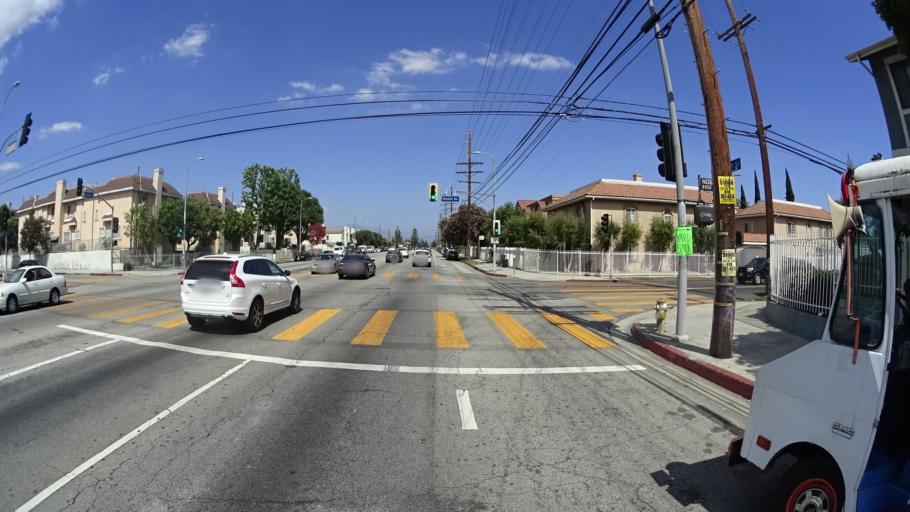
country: US
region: California
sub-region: Los Angeles County
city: Van Nuys
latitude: 34.2354
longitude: -118.4613
